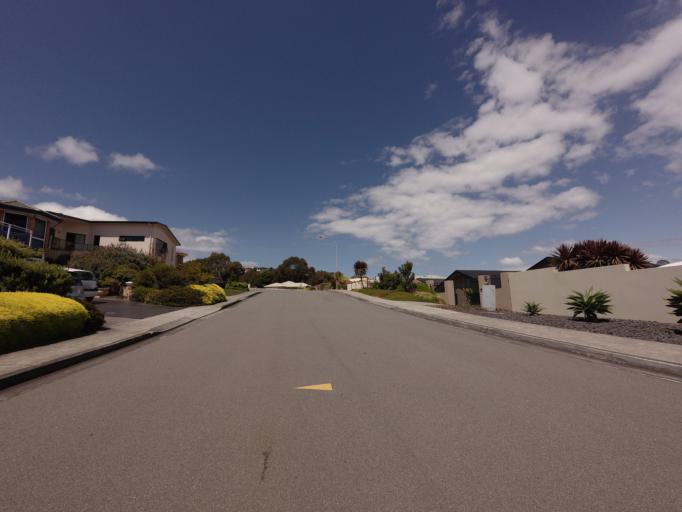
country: AU
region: Tasmania
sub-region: Clarence
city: Howrah
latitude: -42.9201
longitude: 147.4114
